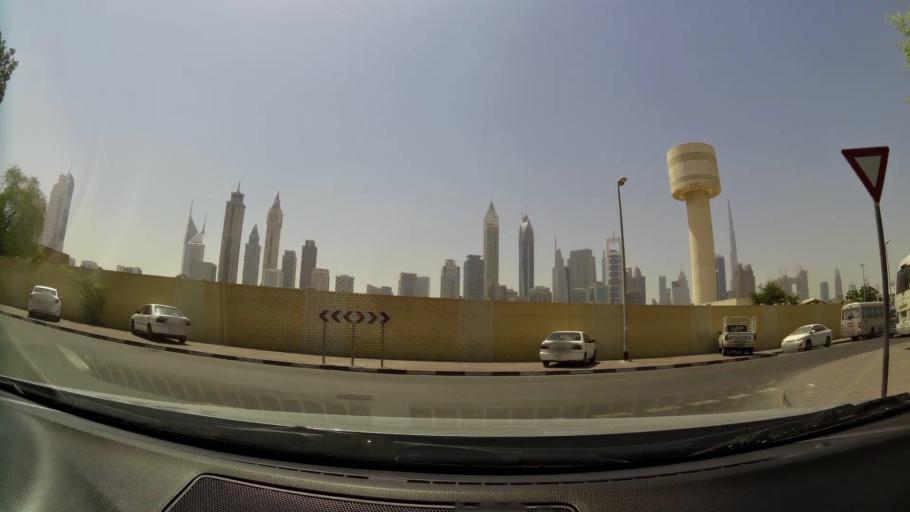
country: AE
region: Dubai
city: Dubai
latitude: 25.2197
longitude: 55.2703
